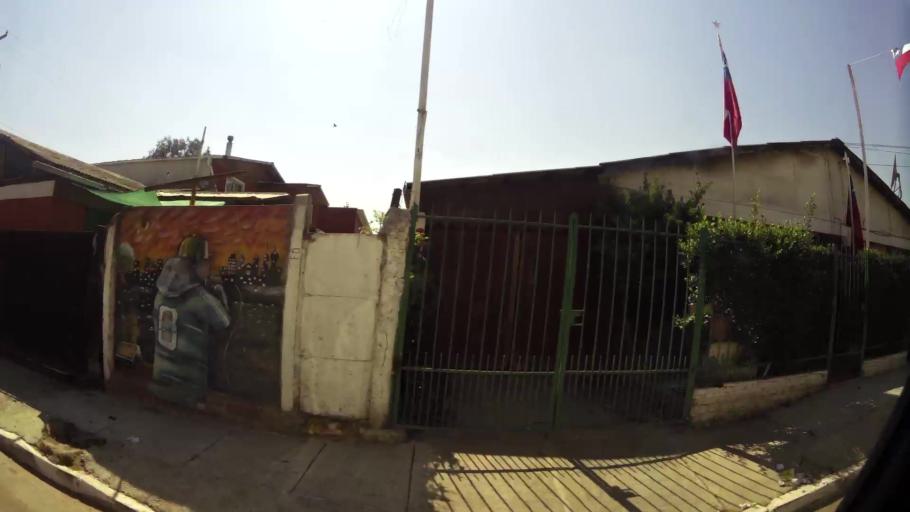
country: CL
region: Santiago Metropolitan
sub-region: Provincia de Talagante
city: Penaflor
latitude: -33.5772
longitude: -70.8111
